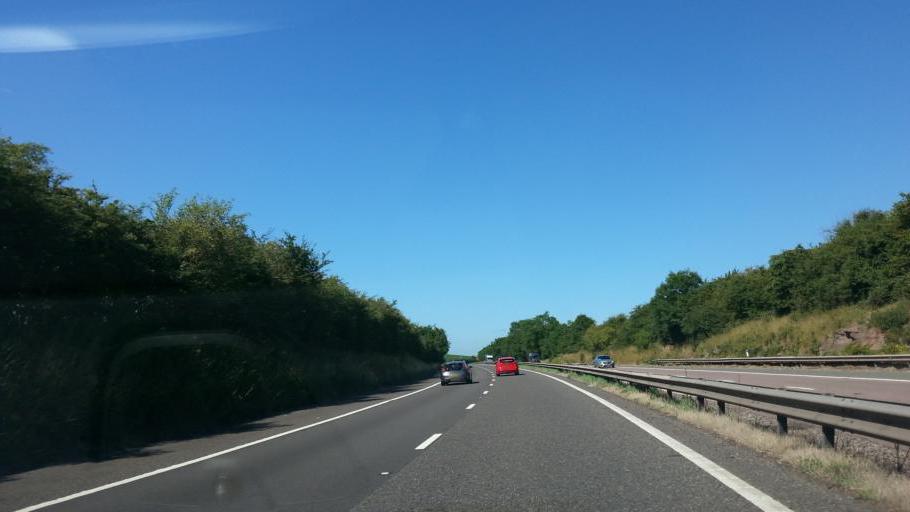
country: GB
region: England
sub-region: Herefordshire
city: Linton
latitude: 51.9316
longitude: -2.5195
